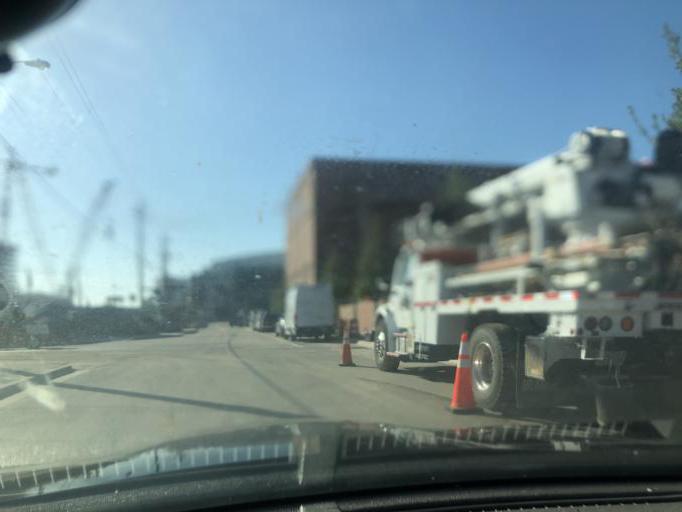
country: US
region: Florida
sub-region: Hillsborough County
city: Tampa
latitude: 27.9460
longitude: -82.4512
